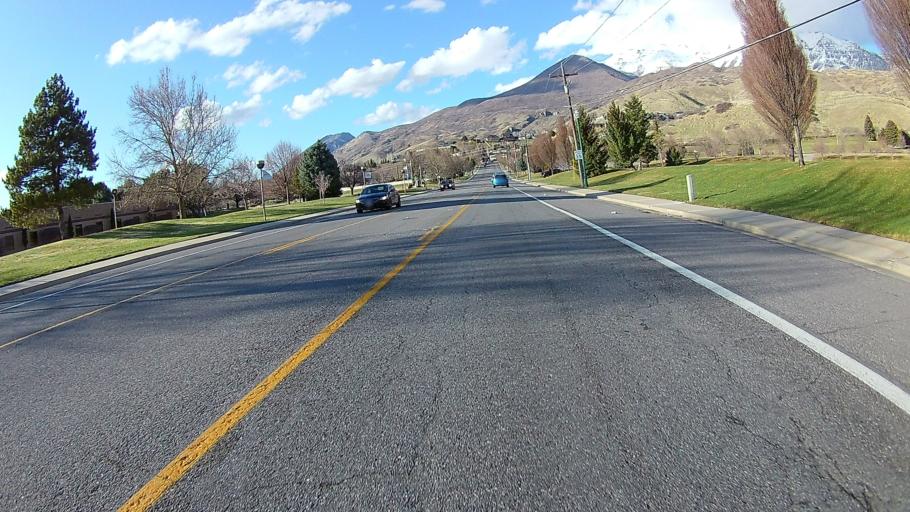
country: US
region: Utah
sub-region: Utah County
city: Orem
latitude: 40.3200
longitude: -111.6768
